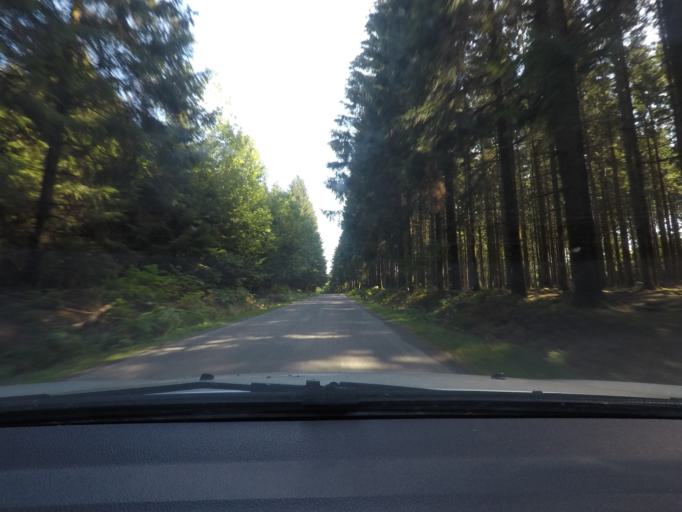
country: BE
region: Wallonia
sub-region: Province du Luxembourg
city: Fauvillers
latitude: 49.8048
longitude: 5.6416
